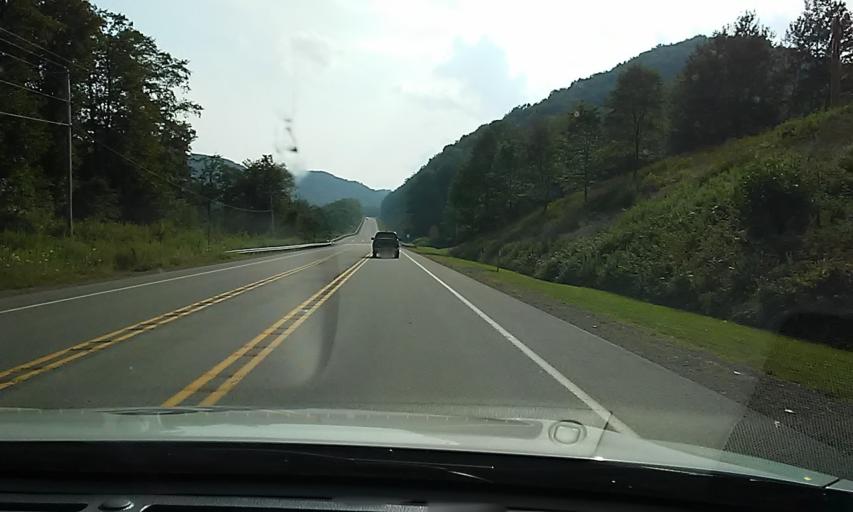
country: US
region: Pennsylvania
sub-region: Potter County
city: Galeton
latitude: 41.7792
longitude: -77.8255
